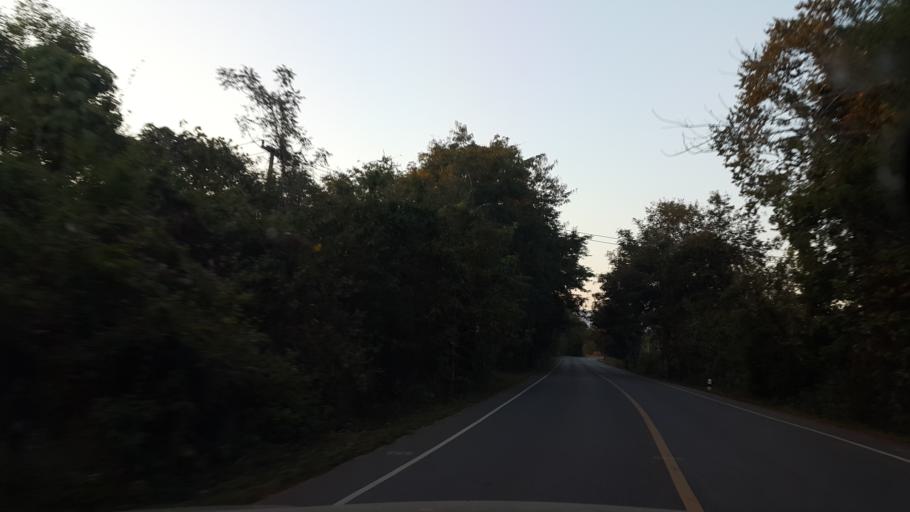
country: TH
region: Phrae
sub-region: Amphoe Wang Chin
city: Wang Chin
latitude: 17.8590
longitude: 99.6260
